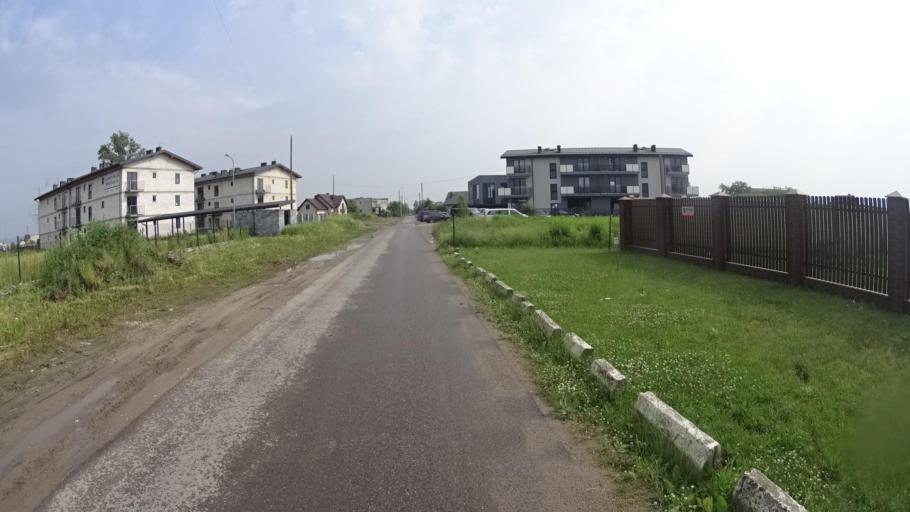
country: PL
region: Masovian Voivodeship
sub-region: Powiat pruszkowski
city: Raszyn
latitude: 52.1670
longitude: 20.9197
